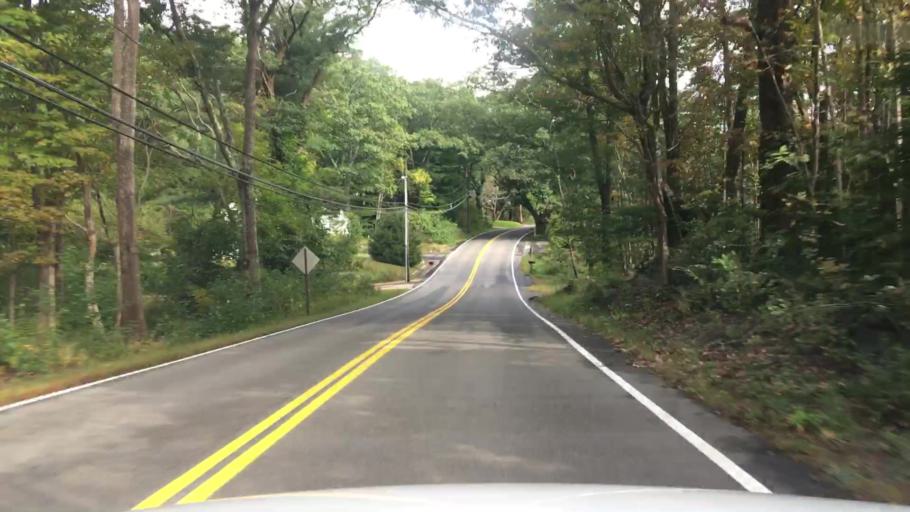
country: US
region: Maine
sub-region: York County
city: Kittery Point
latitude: 43.0937
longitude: -70.6786
